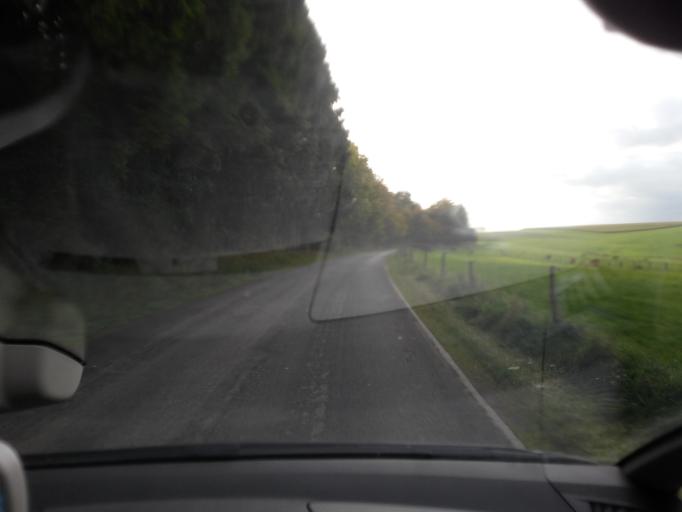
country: BE
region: Wallonia
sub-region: Province du Luxembourg
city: Attert
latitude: 49.7235
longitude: 5.7841
